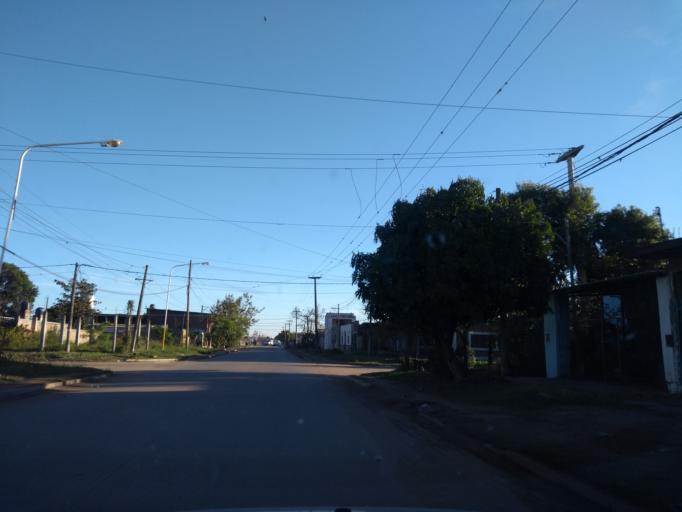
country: AR
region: Chaco
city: Barranqueras
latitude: -27.4932
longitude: -58.9512
